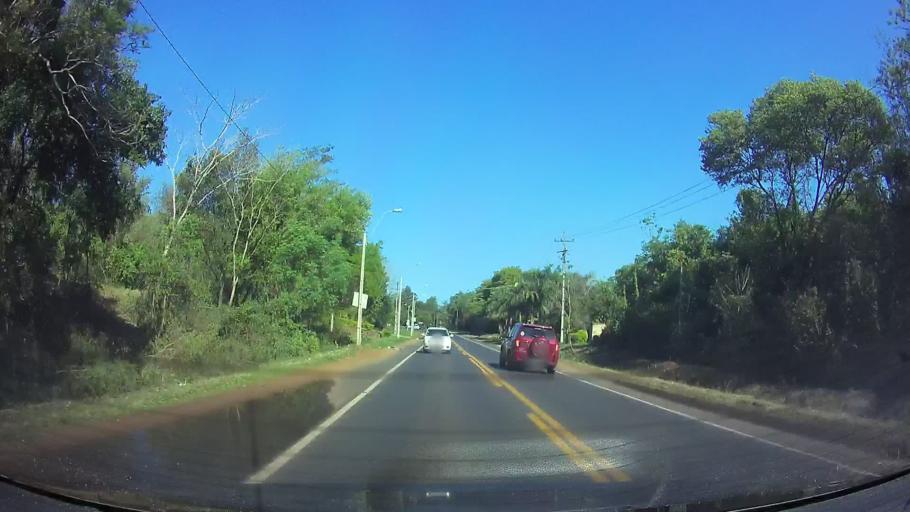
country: PY
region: Central
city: Aregua
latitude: -25.3390
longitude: -57.3498
